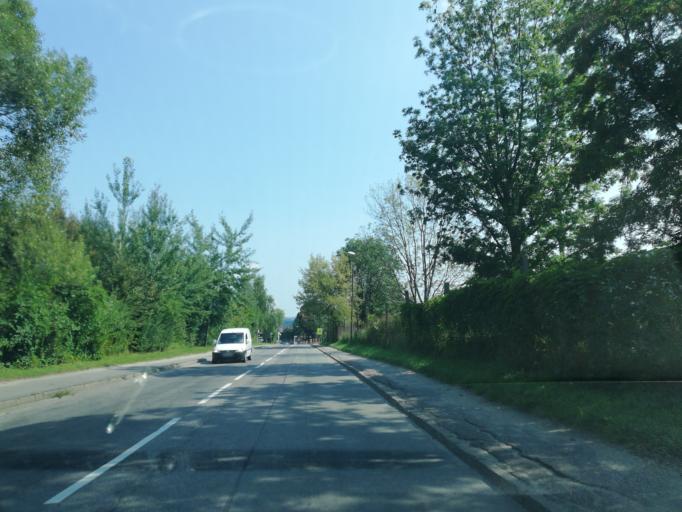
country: PL
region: Lesser Poland Voivodeship
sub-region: Powiat nowosadecki
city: Nowy Sacz
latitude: 49.6019
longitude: 20.7101
